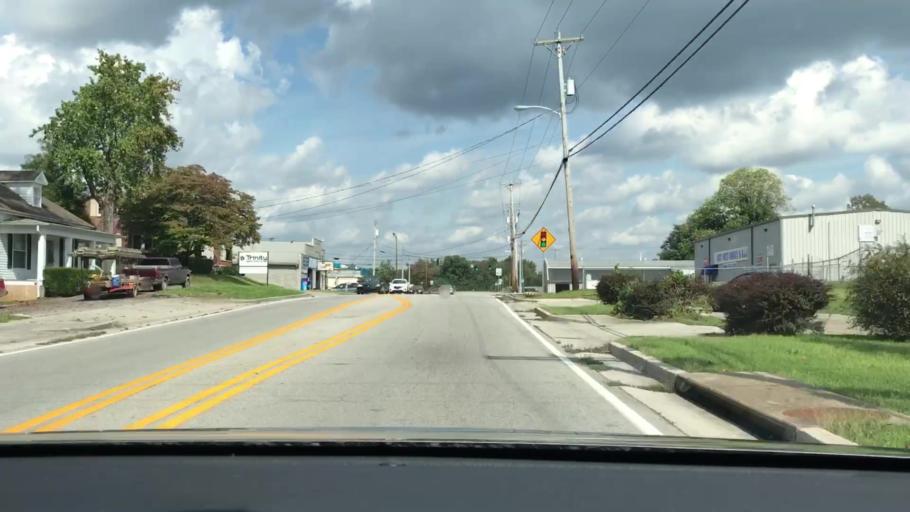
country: US
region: Kentucky
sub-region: Pulaski County
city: Somerset
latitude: 37.0745
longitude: -84.6156
